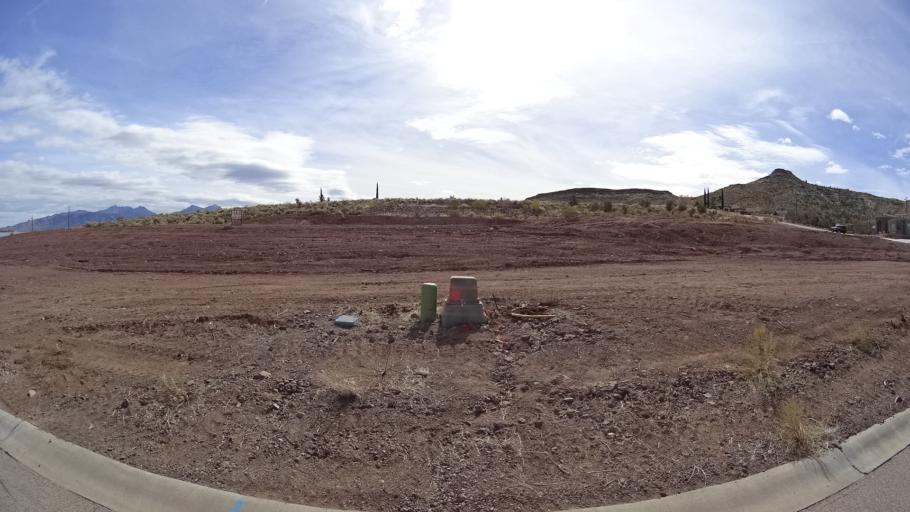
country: US
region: Arizona
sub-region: Mohave County
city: New Kingman-Butler
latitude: 35.2312
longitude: -114.0568
